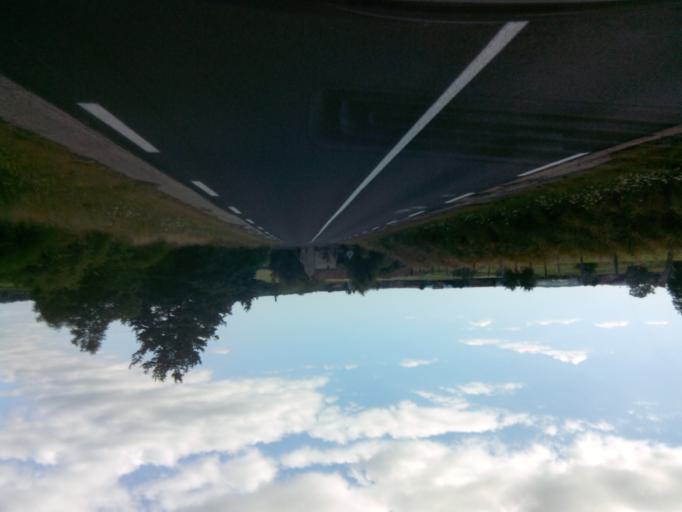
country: FR
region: Auvergne
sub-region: Departement de la Haute-Loire
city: Saint-Paulien
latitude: 45.1885
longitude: 3.8236
